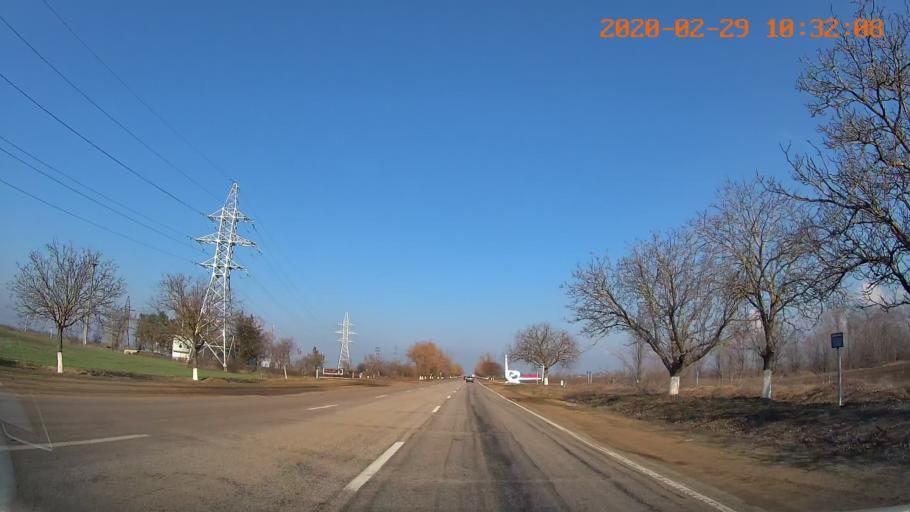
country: UA
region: Odessa
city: Velykoploske
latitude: 46.9573
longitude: 29.5563
